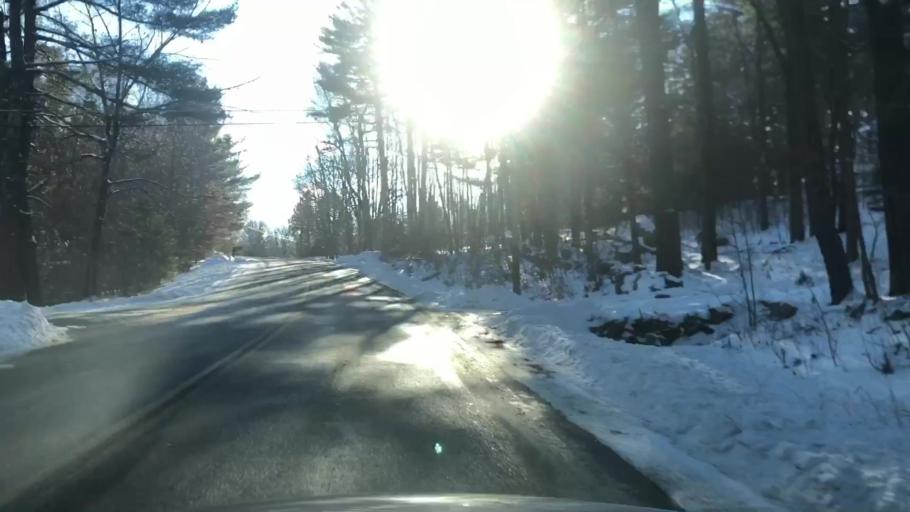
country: US
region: New Hampshire
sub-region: Hillsborough County
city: Wilton
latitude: 42.8187
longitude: -71.7212
